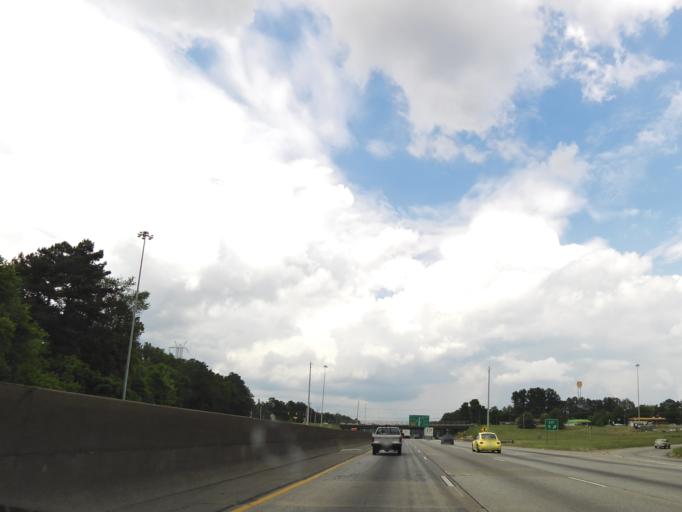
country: US
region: Georgia
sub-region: Fulton County
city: East Point
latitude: 33.7509
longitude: -84.4965
